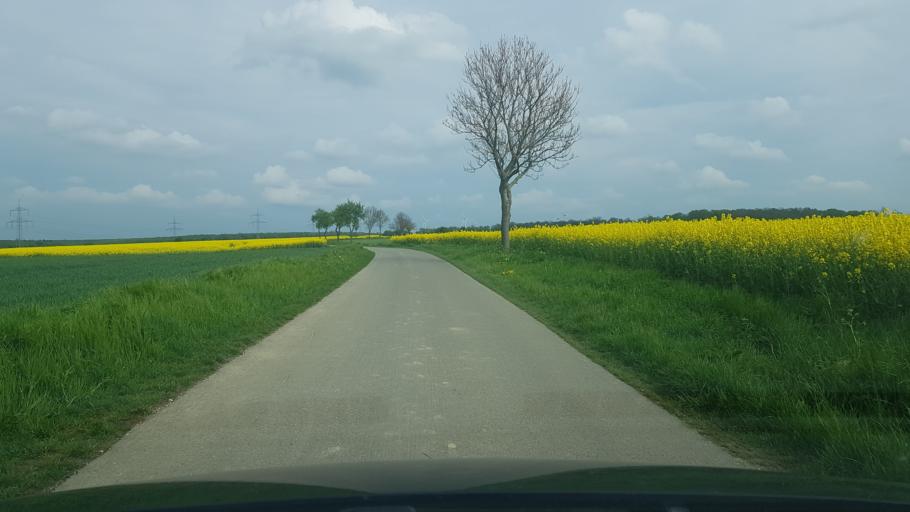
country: DE
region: North Rhine-Westphalia
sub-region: Regierungsbezirk Detmold
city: Paderborn
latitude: 51.6548
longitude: 8.7519
